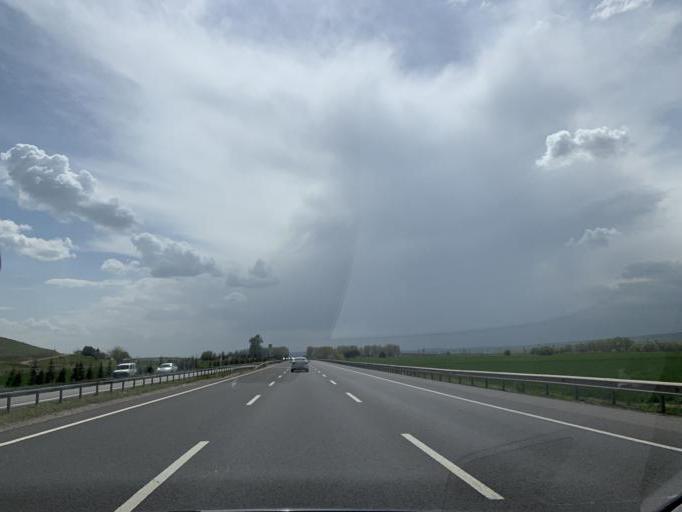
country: TR
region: Ankara
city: Temelli
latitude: 39.6989
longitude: 32.2660
